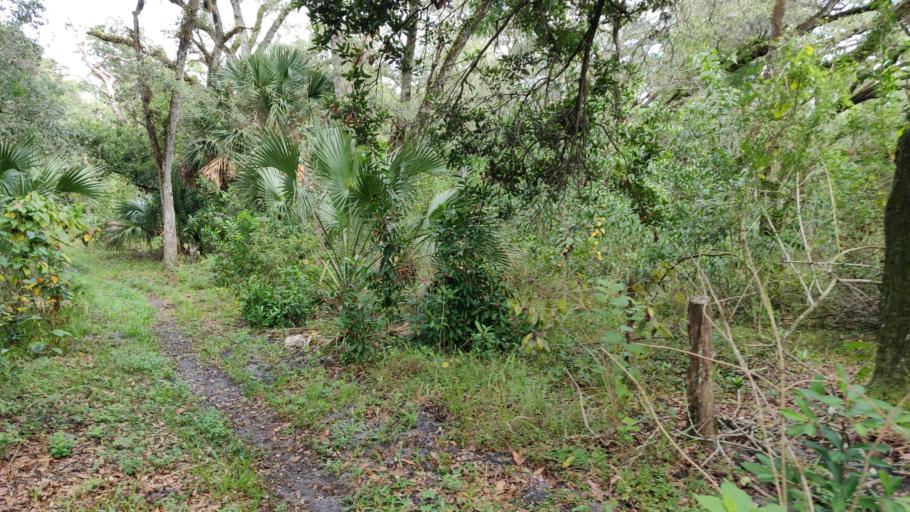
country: US
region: Florida
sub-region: Broward County
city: Cooper City
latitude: 26.0745
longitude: -80.2739
